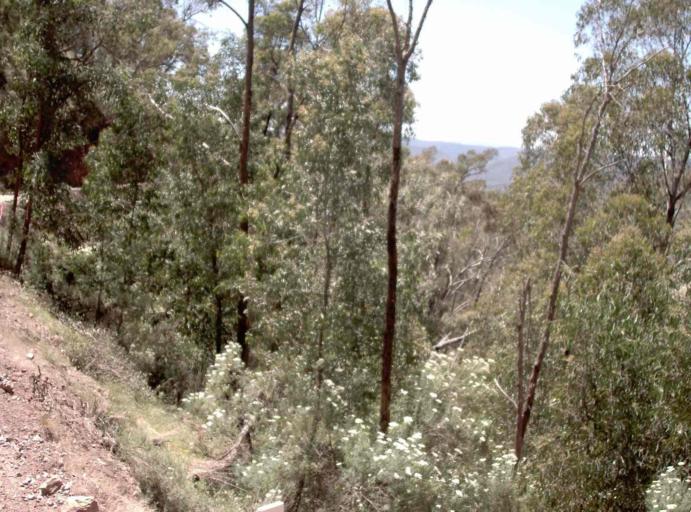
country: AU
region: New South Wales
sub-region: Snowy River
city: Jindabyne
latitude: -36.9895
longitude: 148.3002
